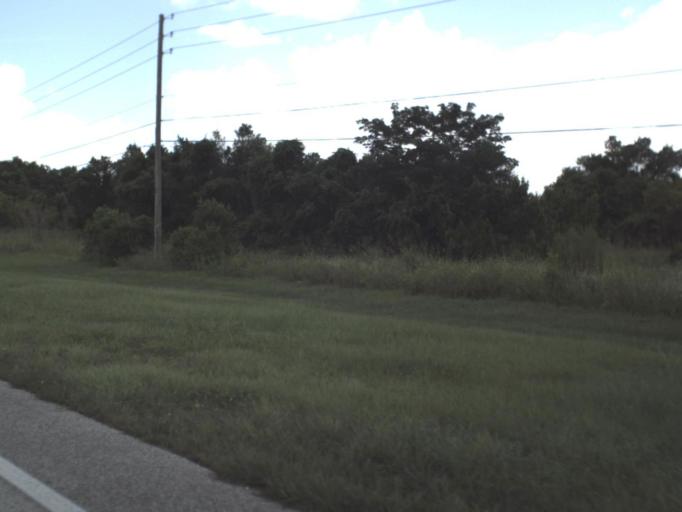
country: US
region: Florida
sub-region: Polk County
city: Eagle Lake
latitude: 27.9704
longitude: -81.7670
